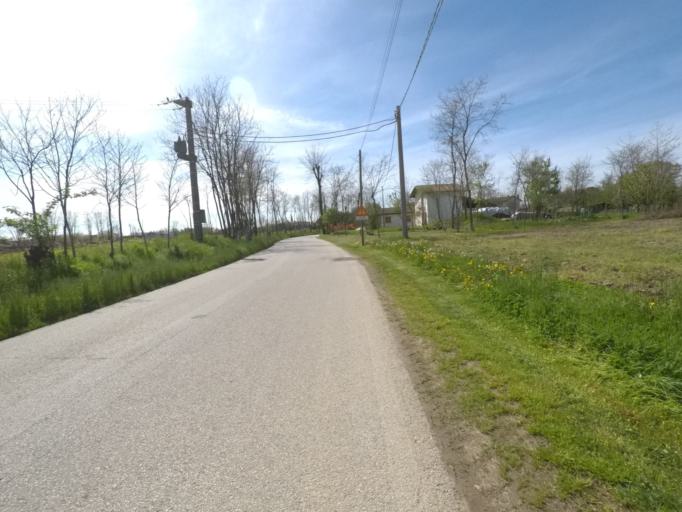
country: IT
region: Friuli Venezia Giulia
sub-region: Provincia di Pordenone
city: Orcenico Inferiore
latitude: 45.9453
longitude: 12.7654
